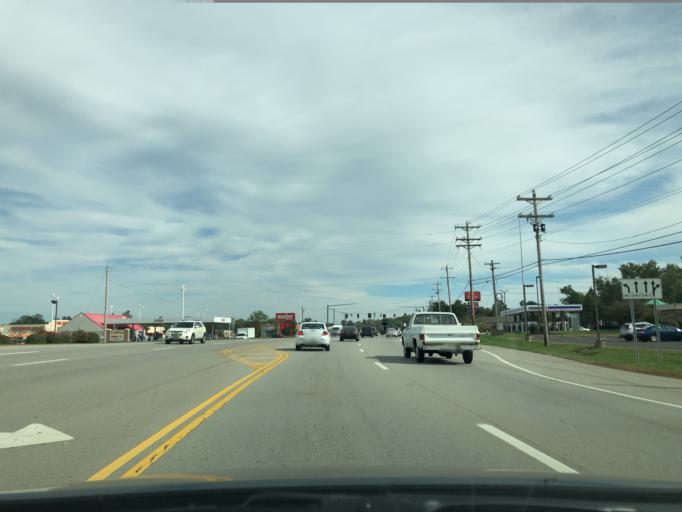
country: US
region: Ohio
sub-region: Clermont County
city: Mulberry
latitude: 39.1947
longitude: -84.2367
